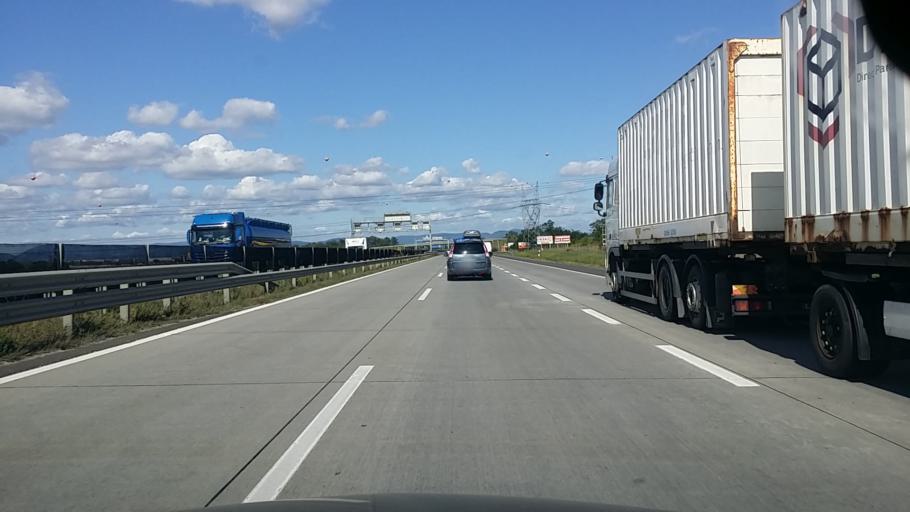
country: HU
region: Budapest
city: Budapest XVI. keruelet
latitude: 47.5588
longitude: 19.1747
